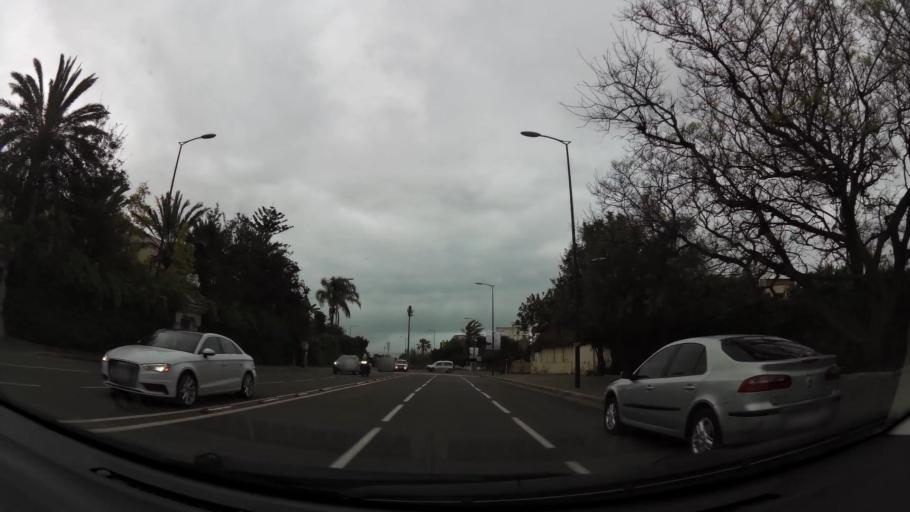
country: MA
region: Grand Casablanca
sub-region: Casablanca
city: Casablanca
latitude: 33.5933
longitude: -7.6610
